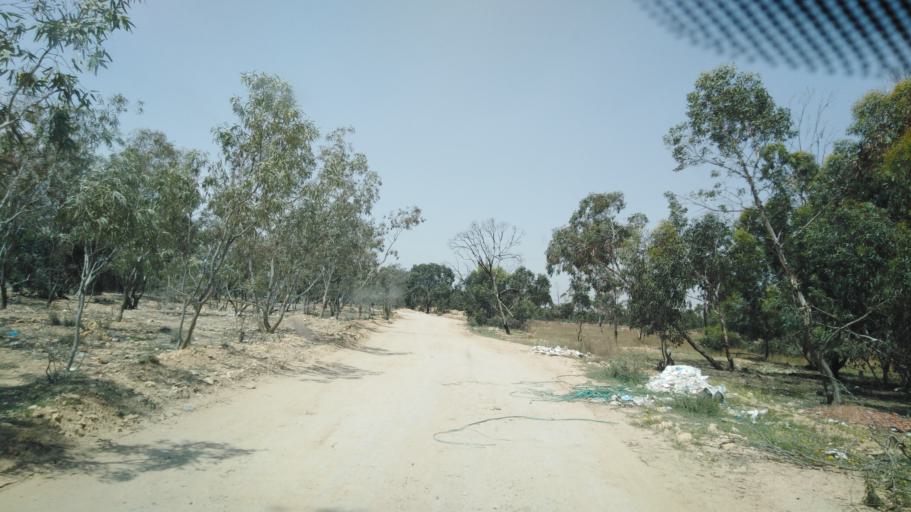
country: TN
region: Safaqis
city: Sfax
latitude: 34.7210
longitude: 10.5755
